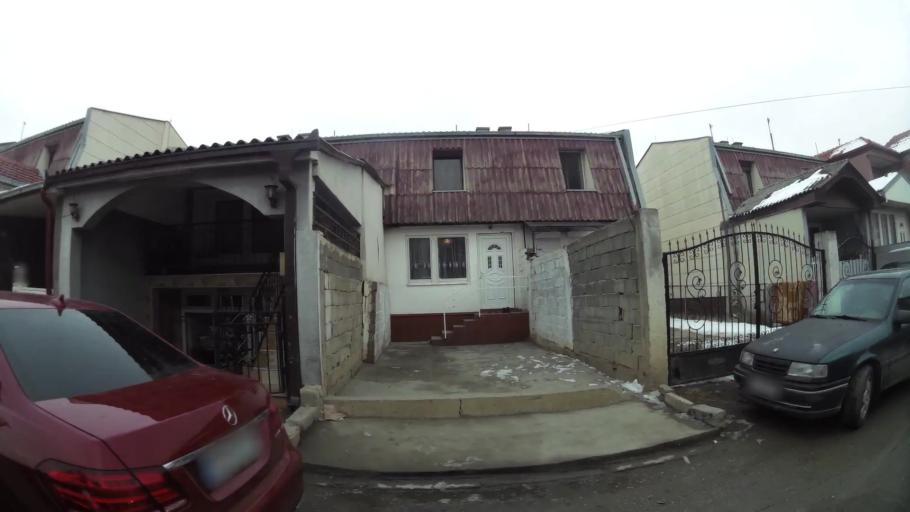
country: MK
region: Suto Orizari
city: Suto Orizare
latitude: 42.0416
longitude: 21.4219
